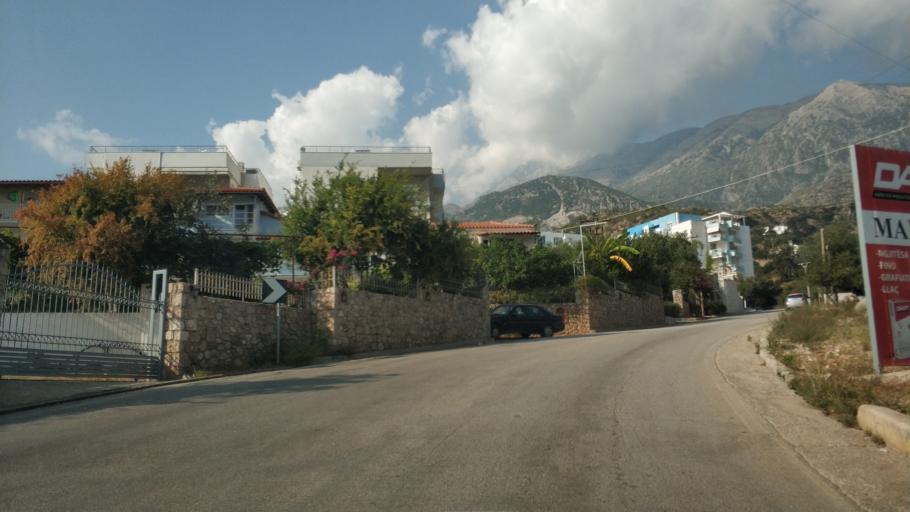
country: AL
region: Vlore
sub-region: Rrethi i Vlores
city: Vranisht
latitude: 40.1486
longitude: 19.6339
